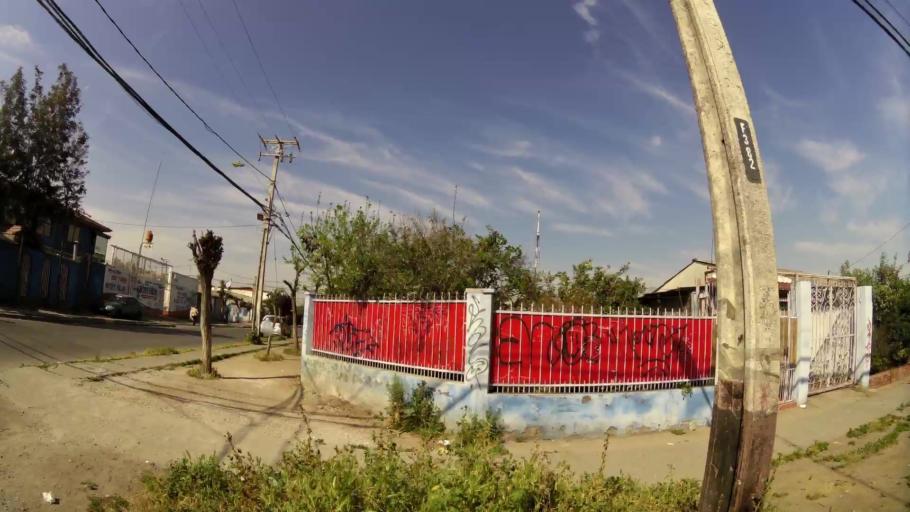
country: CL
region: Santiago Metropolitan
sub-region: Provincia de Santiago
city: La Pintana
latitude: -33.5589
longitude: -70.6641
